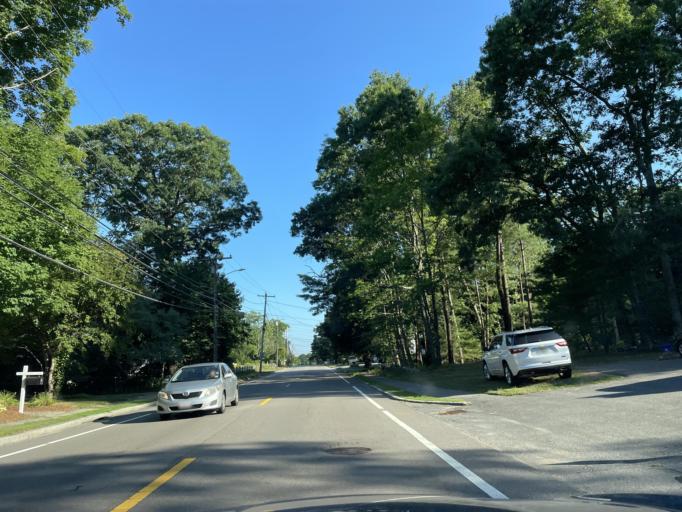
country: US
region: Massachusetts
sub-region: Bristol County
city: Mansfield
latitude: 42.0410
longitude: -71.2335
